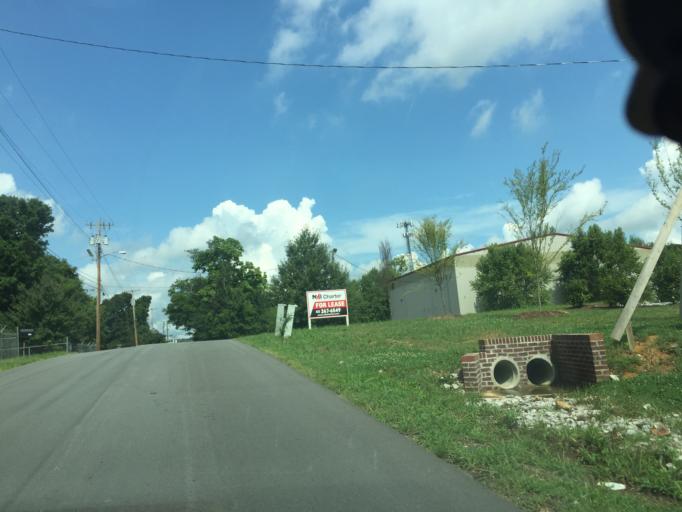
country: US
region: Tennessee
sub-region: Hamilton County
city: East Chattanooga
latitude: 35.0718
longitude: -85.2647
